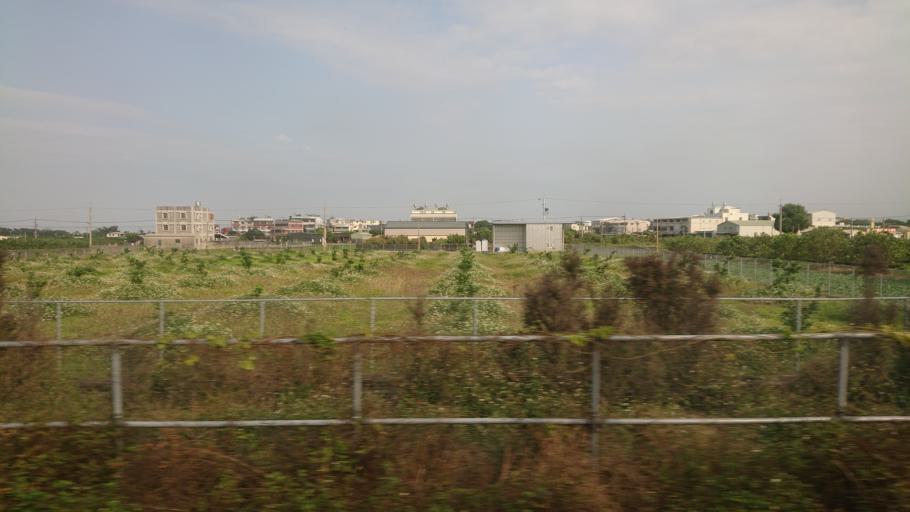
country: TW
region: Taiwan
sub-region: Yunlin
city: Douliu
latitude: 23.7151
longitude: 120.5578
